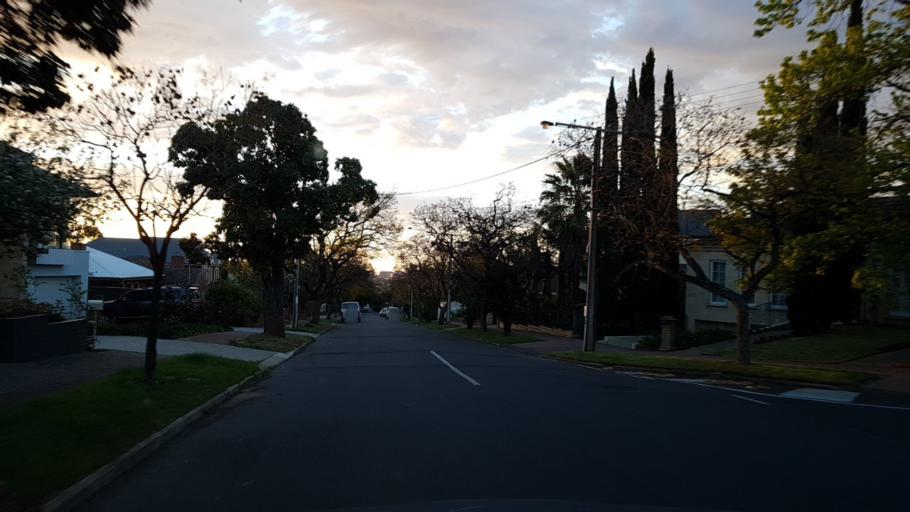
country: AU
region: South Australia
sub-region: Burnside
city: Glenunga
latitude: -34.9498
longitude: 138.6455
